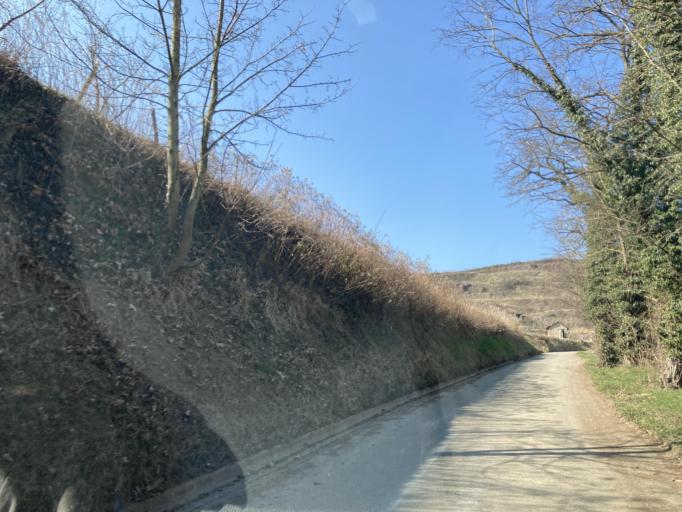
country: DE
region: Baden-Wuerttemberg
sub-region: Freiburg Region
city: Ihringen
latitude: 48.0578
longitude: 7.6415
